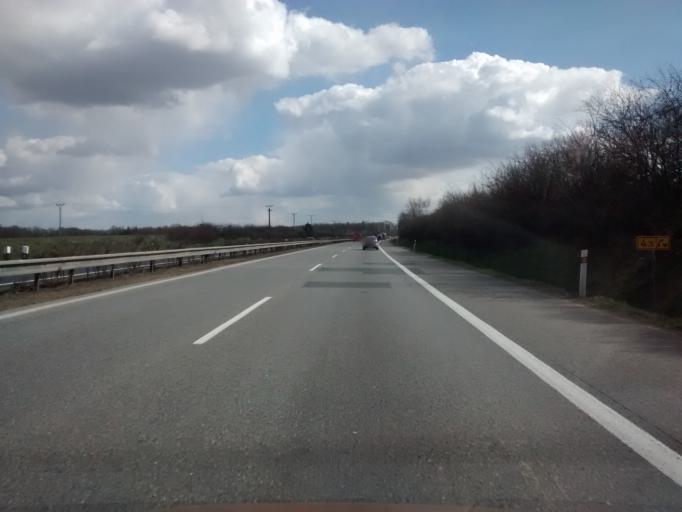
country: CZ
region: Central Bohemia
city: Odolena Voda
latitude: 50.2181
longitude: 14.4218
